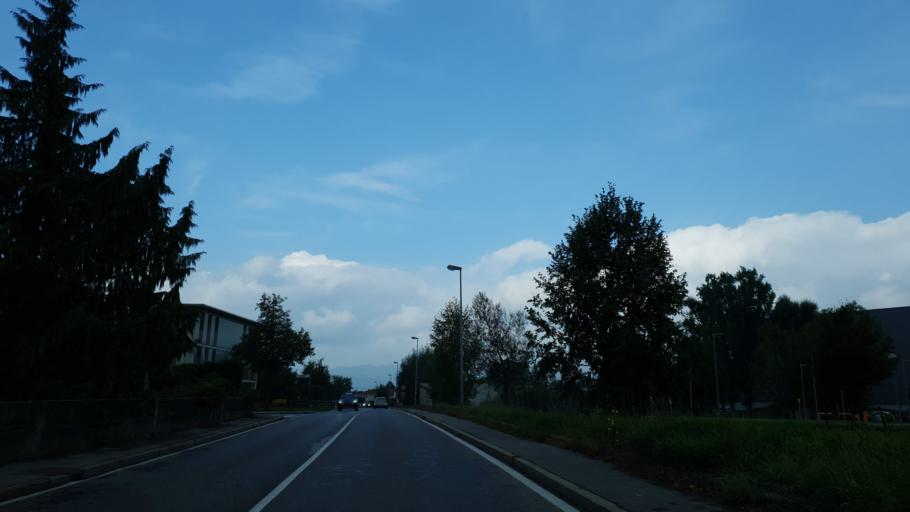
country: AT
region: Vorarlberg
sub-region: Politischer Bezirk Dornbirn
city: Dornbirn
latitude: 47.3978
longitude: 9.7235
